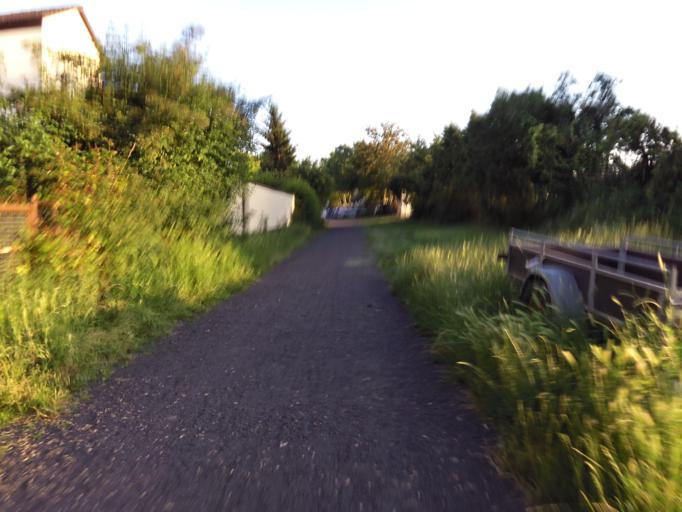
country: DE
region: Rheinland-Pfalz
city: Beindersheim
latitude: 49.5603
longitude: 8.3146
